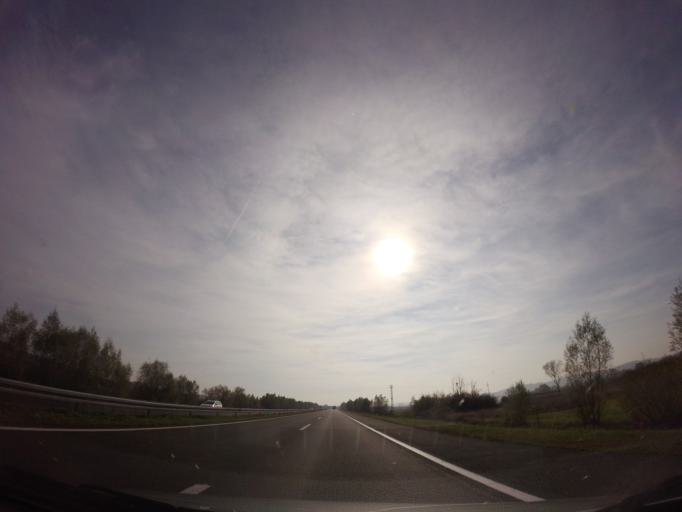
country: HR
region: Zagrebacka
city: Brckovljani
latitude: 45.9691
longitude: 16.2839
